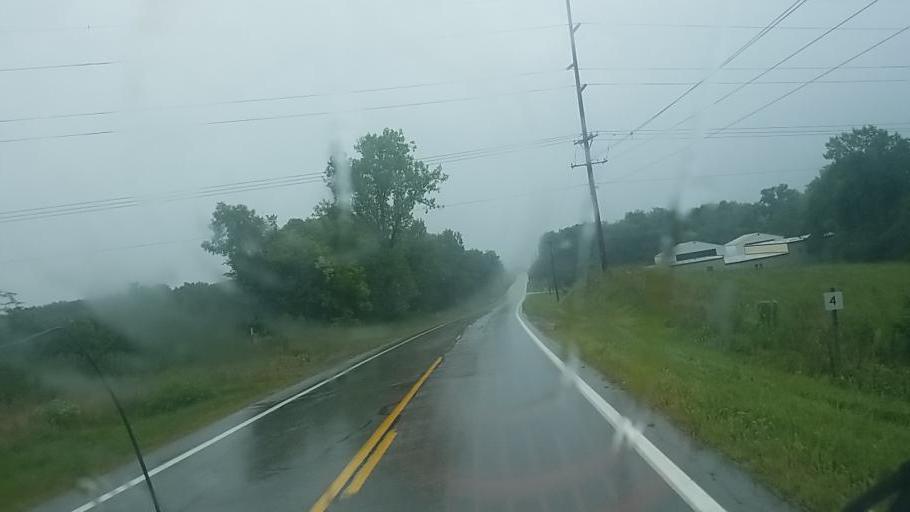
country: US
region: Ohio
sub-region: Champaign County
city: North Lewisburg
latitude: 40.3275
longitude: -83.5982
